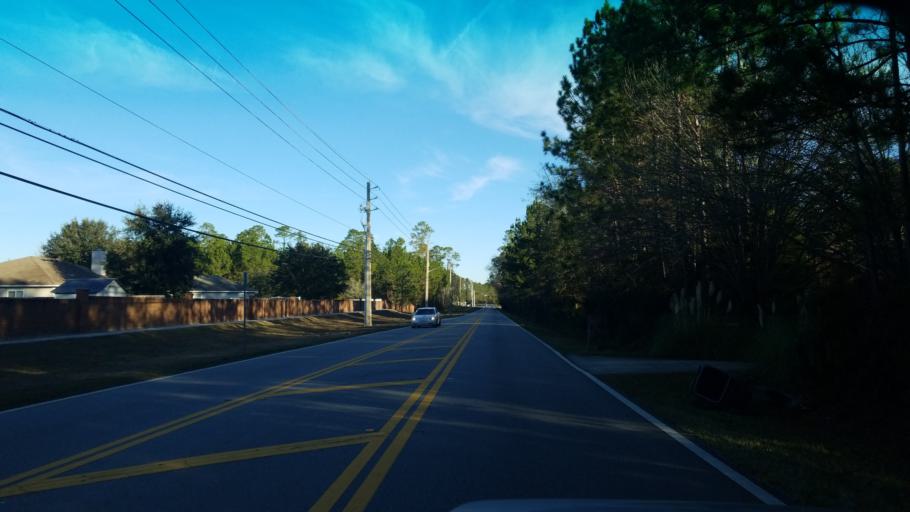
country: US
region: Florida
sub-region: Duval County
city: Baldwin
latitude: 30.3287
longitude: -81.8486
